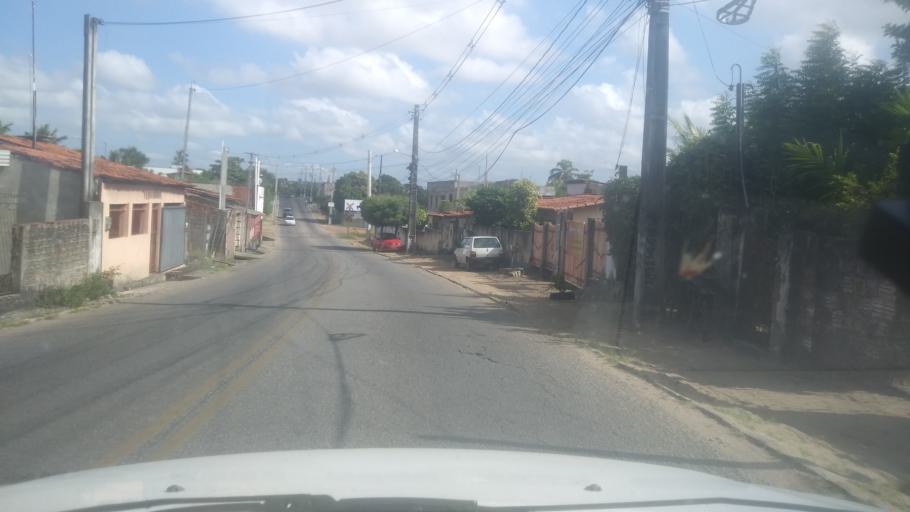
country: BR
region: Rio Grande do Norte
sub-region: Extremoz
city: Extremoz
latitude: -5.7097
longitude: -35.2780
